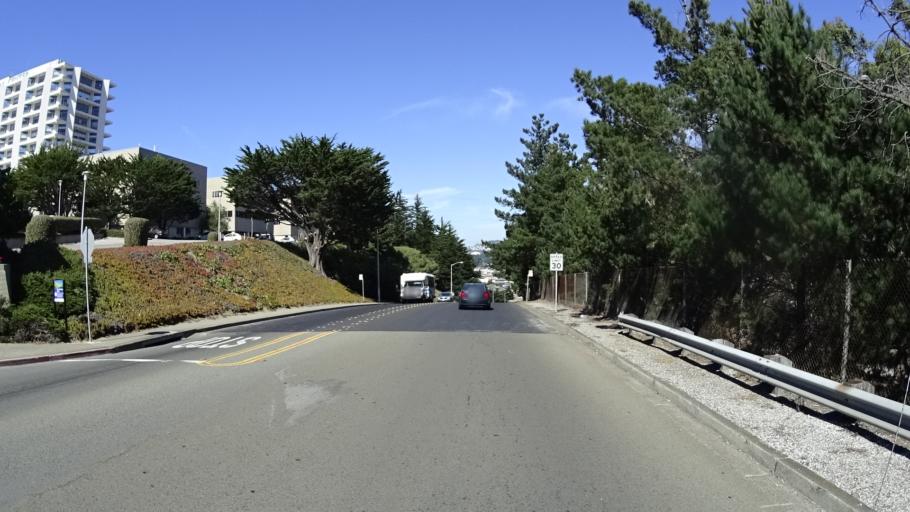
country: US
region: California
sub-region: San Mateo County
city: Broadmoor
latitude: 37.6789
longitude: -122.4730
